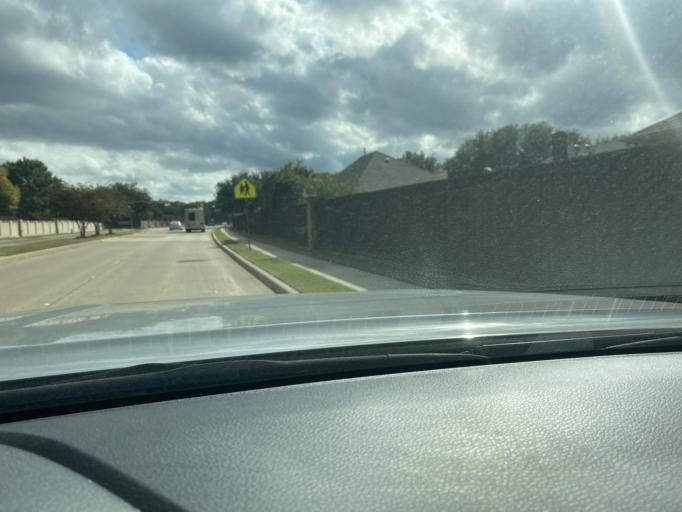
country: US
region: Texas
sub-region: Collin County
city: Plano
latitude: 33.0522
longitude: -96.7886
